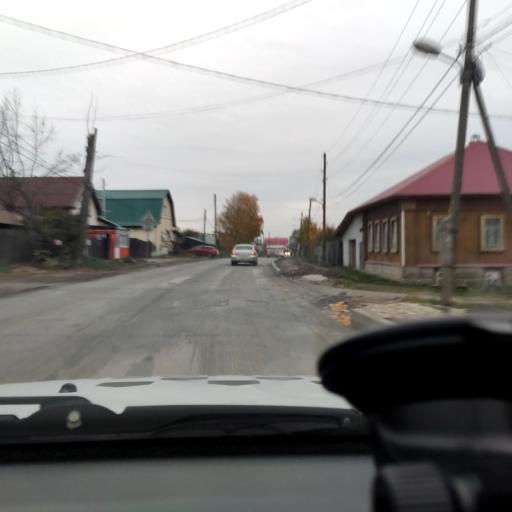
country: RU
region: Perm
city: Kondratovo
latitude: 57.9608
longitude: 56.1252
